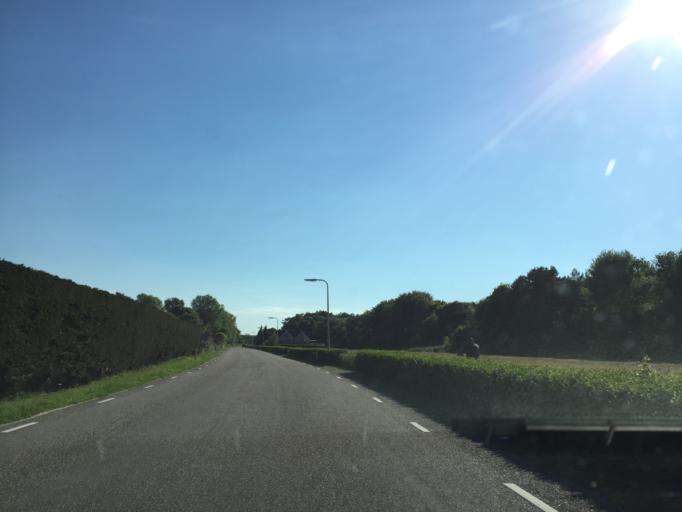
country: NL
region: South Holland
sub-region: Gemeente Noordwijkerhout
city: Noordwijkerhout
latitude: 52.2671
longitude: 4.4637
